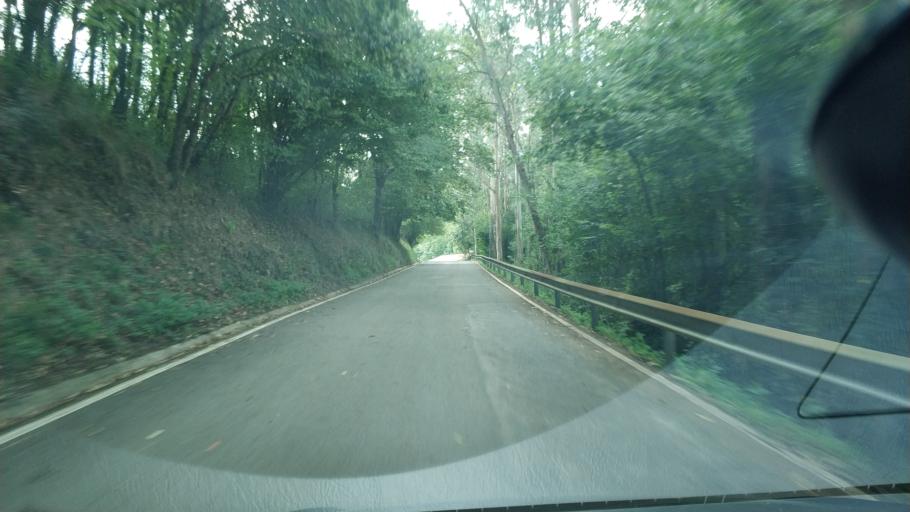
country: ES
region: Cantabria
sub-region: Provincia de Cantabria
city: Santa Maria de Cayon
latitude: 43.2844
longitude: -3.8153
